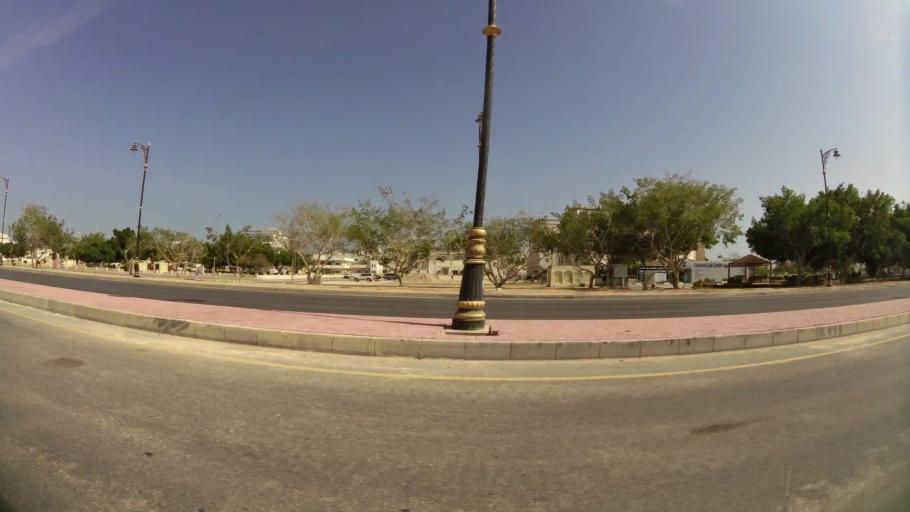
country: OM
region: Zufar
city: Salalah
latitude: 17.0233
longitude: 54.0760
